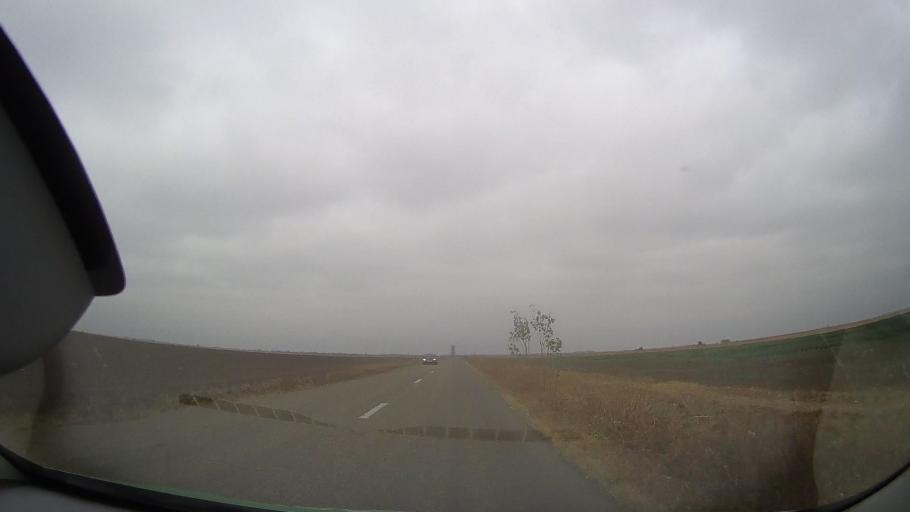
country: RO
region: Buzau
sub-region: Comuna Bradeanu
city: Bradeanu
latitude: 44.8985
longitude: 26.8725
